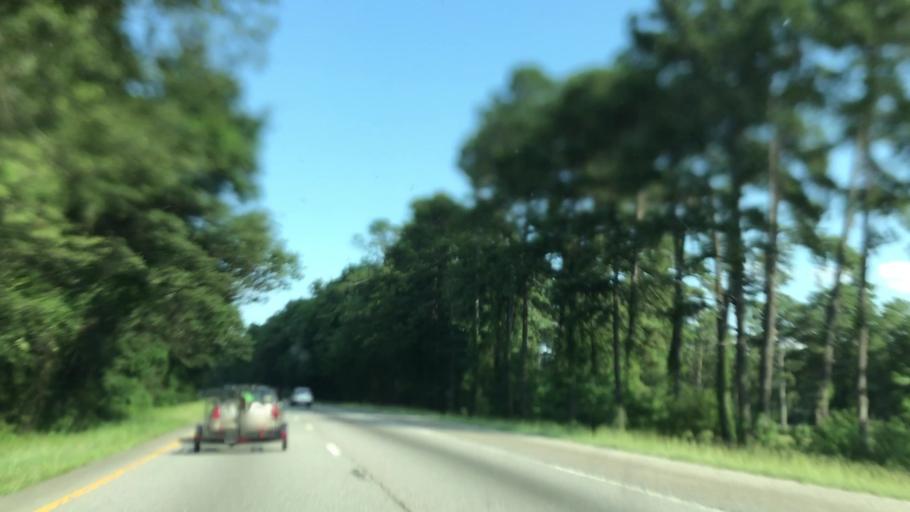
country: US
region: South Carolina
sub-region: Orangeburg County
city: Brookdale
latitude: 33.4682
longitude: -80.7437
